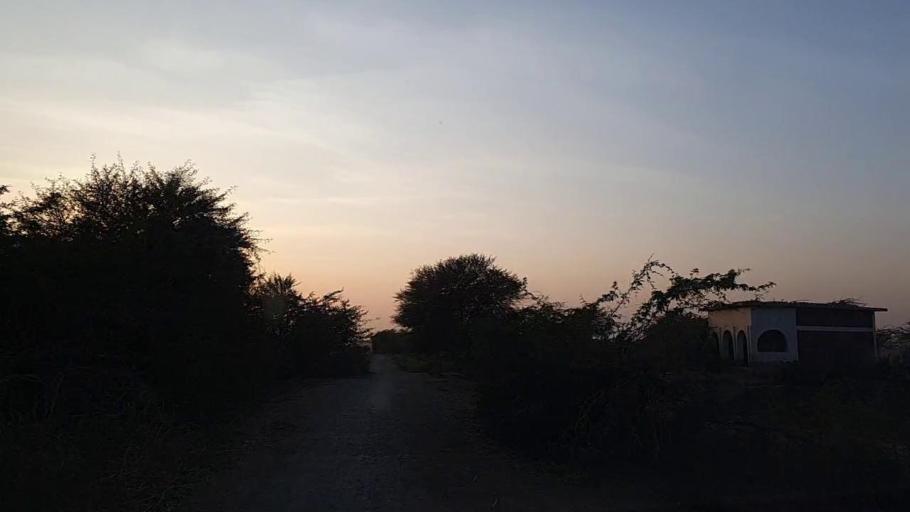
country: PK
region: Sindh
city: Naukot
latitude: 24.9531
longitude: 69.4266
